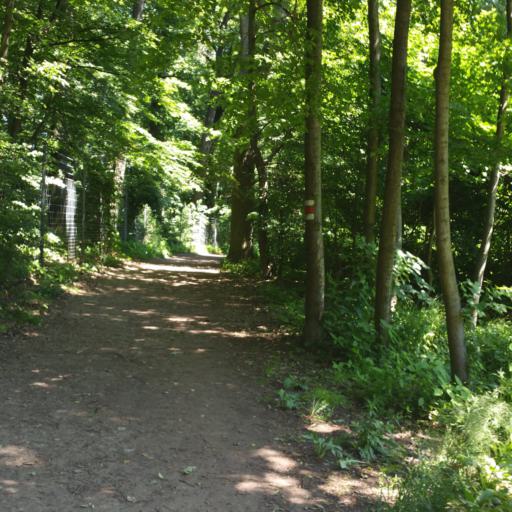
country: AT
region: Vienna
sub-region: Wien Stadt
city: Vienna
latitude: 48.2191
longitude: 16.2797
